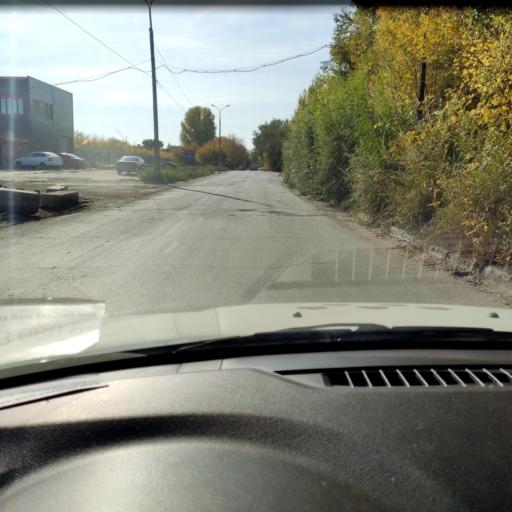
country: RU
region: Samara
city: Tol'yatti
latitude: 53.5574
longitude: 49.3098
